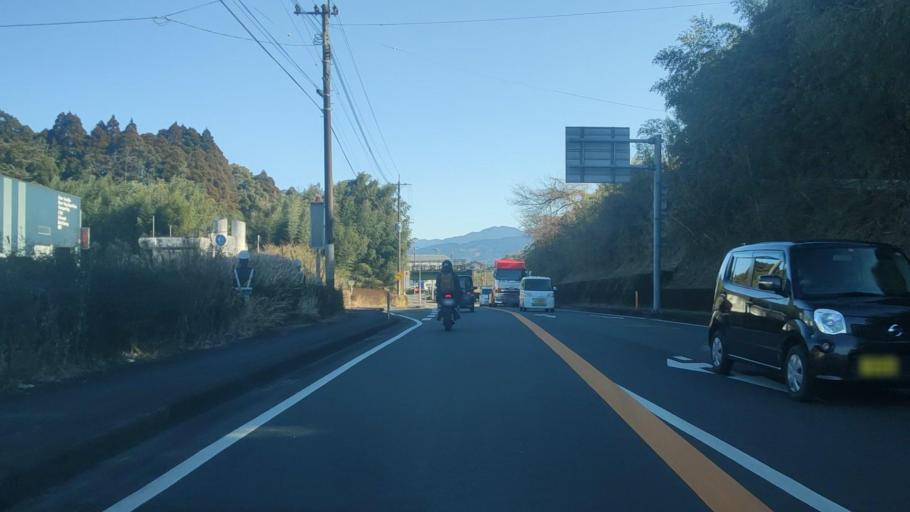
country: JP
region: Miyazaki
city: Miyakonojo
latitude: 31.7097
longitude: 131.0528
